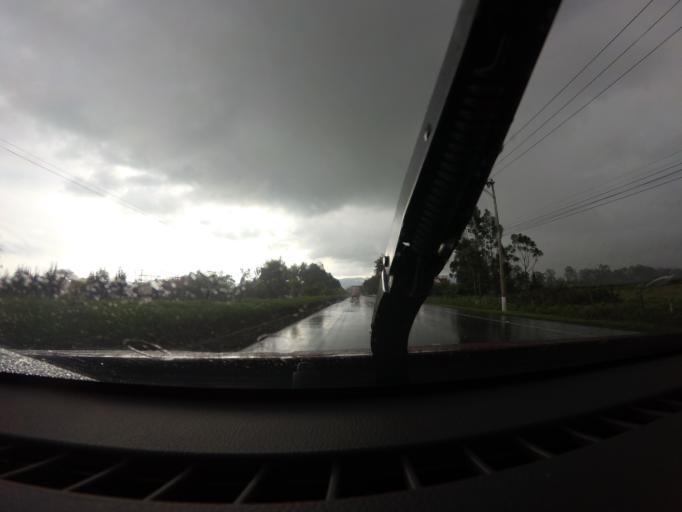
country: CO
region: Cundinamarca
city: El Rosal
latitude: 4.8279
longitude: -74.2411
